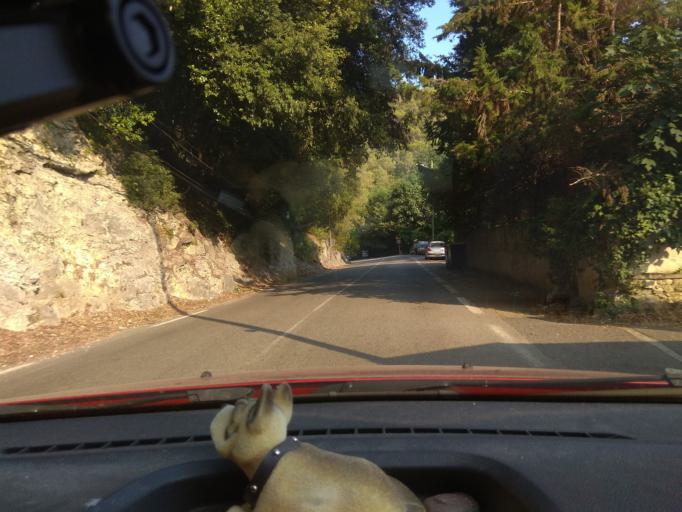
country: FR
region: Provence-Alpes-Cote d'Azur
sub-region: Departement des Alpes-Maritimes
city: La Colle-sur-Loup
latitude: 43.6831
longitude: 7.0887
